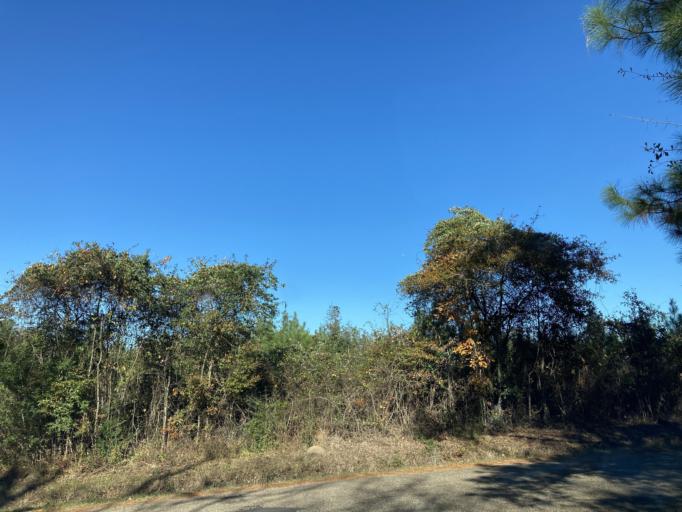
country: US
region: Mississippi
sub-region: Lamar County
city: Sumrall
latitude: 31.3025
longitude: -89.6368
